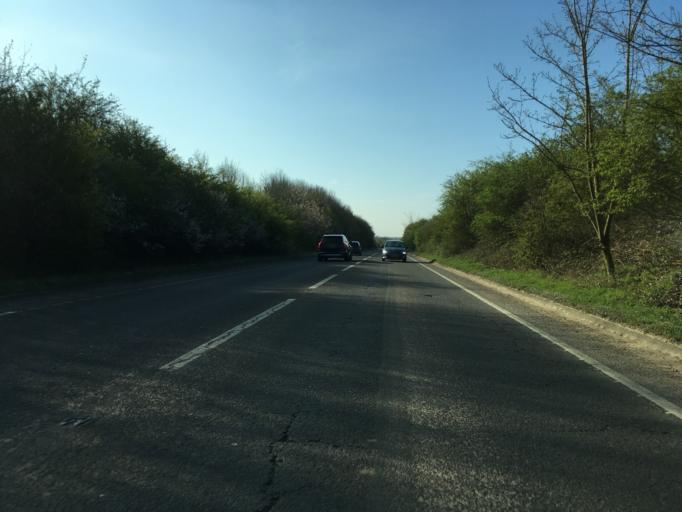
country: GB
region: England
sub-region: Northamptonshire
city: Deanshanger
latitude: 52.0615
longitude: -0.8717
